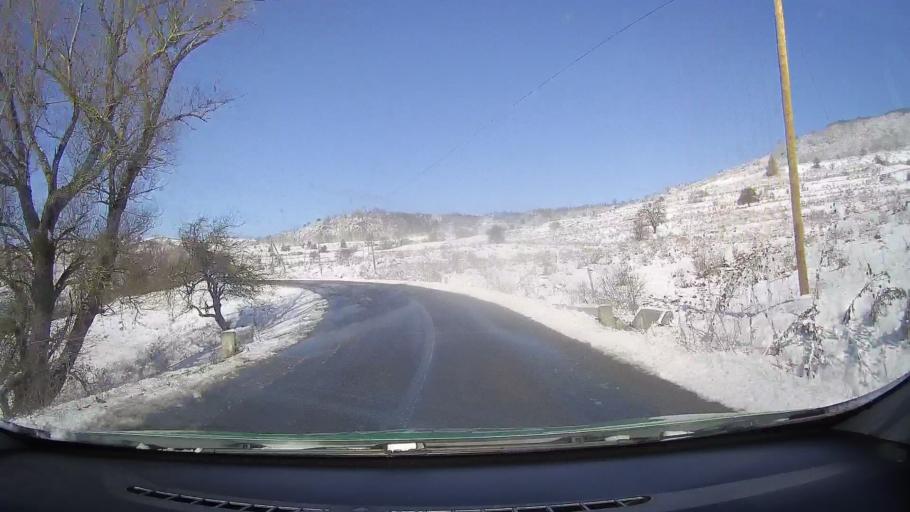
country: RO
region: Sibiu
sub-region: Comuna Avrig
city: Avrig
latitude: 45.7737
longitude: 24.3825
